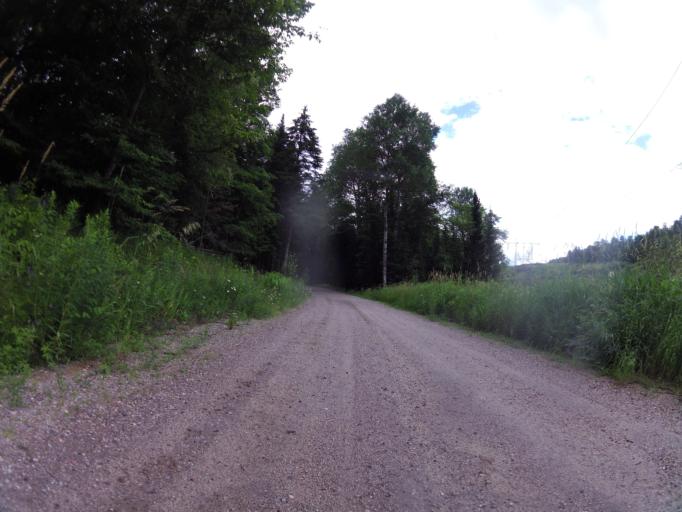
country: CA
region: Ontario
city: Renfrew
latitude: 45.0756
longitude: -76.7223
